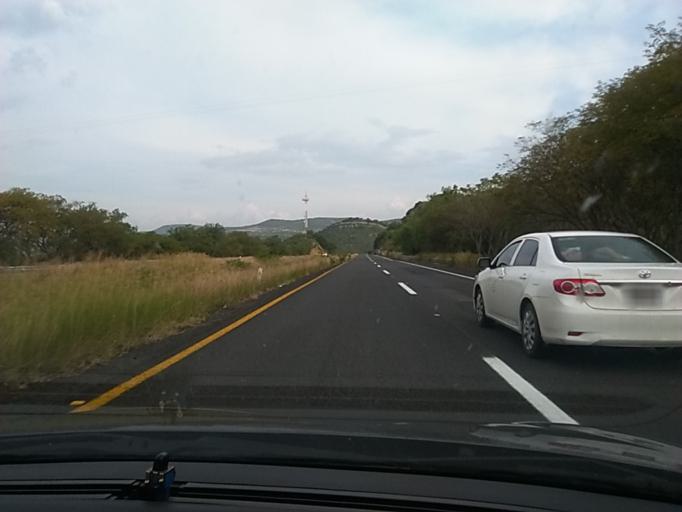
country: MX
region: Michoacan
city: Copandaro de Galeana
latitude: 19.8877
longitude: -101.2305
